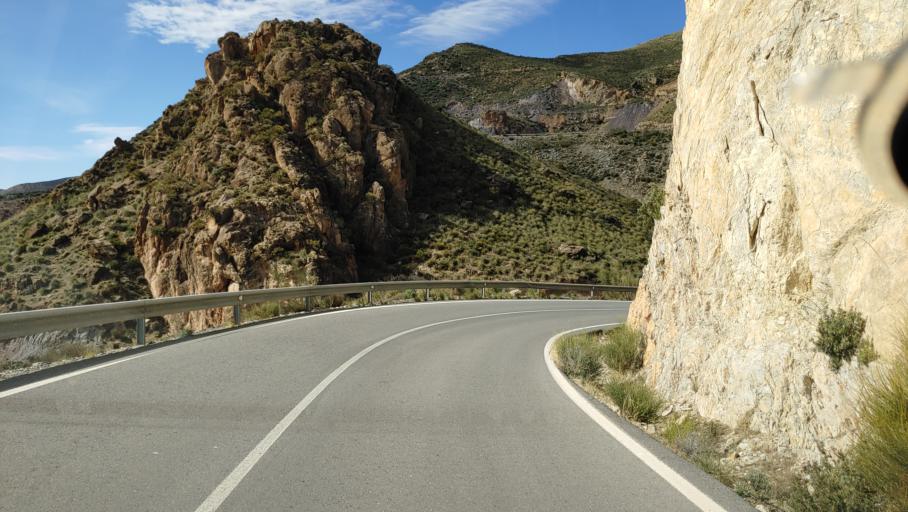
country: ES
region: Andalusia
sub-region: Provincia de Almeria
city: Canjayar
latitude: 37.0241
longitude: -2.7261
